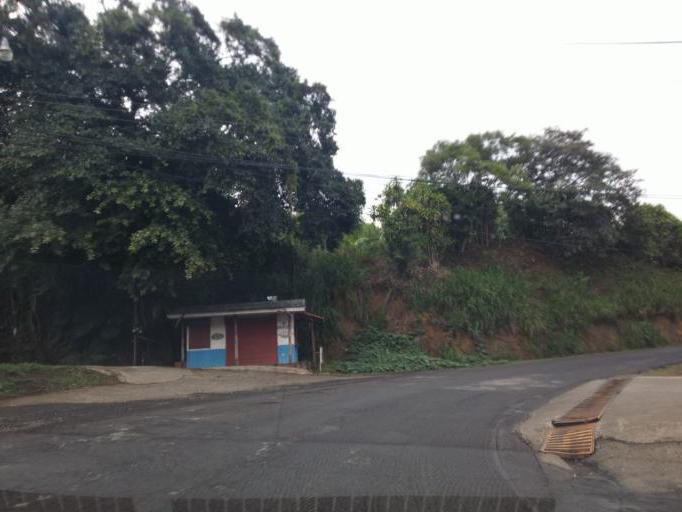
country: CR
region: Alajuela
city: San Juan
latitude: 10.0830
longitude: -84.3362
